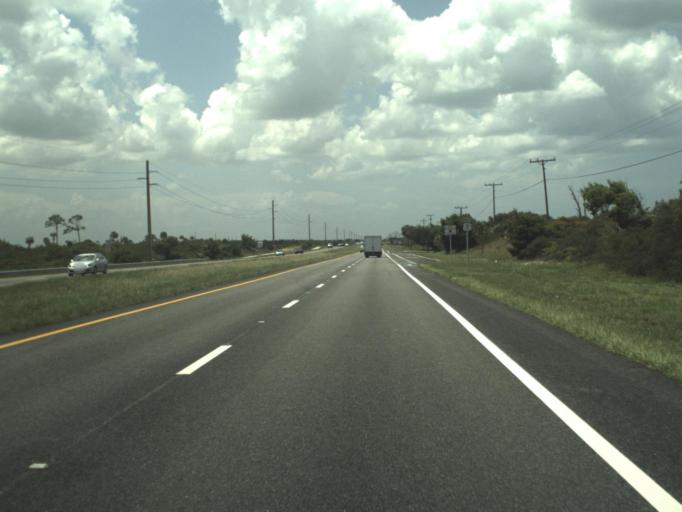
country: US
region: Florida
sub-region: Palm Beach County
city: Tequesta
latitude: 26.9971
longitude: -80.0972
